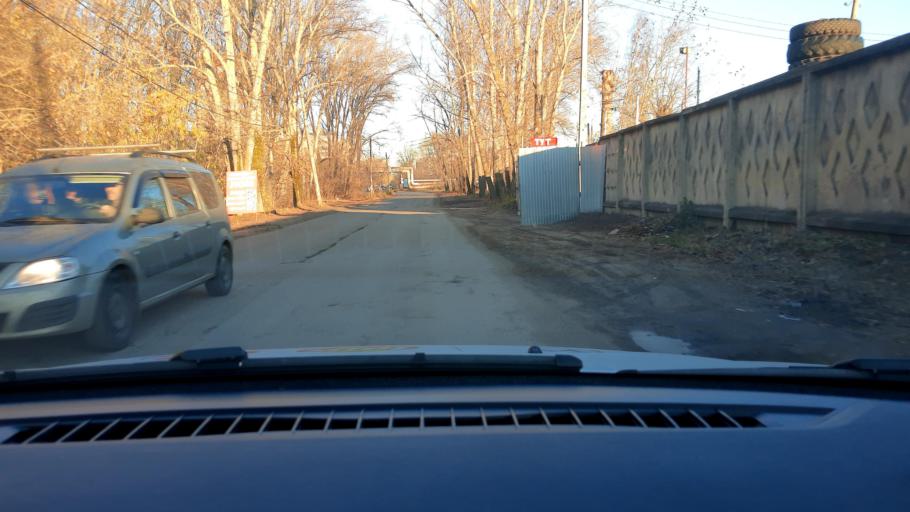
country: RU
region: Nizjnij Novgorod
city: Burevestnik
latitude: 56.2270
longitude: 43.8866
